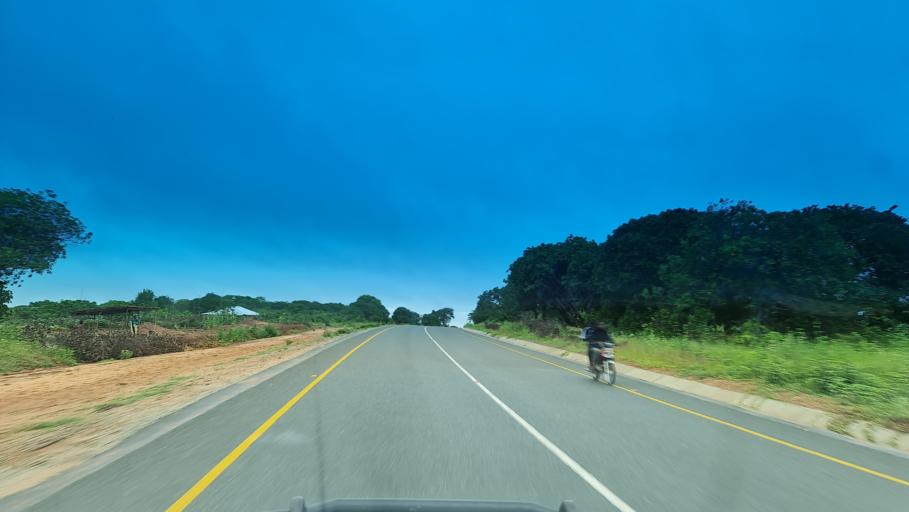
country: MZ
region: Nampula
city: Nampula
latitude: -15.6147
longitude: 39.3322
